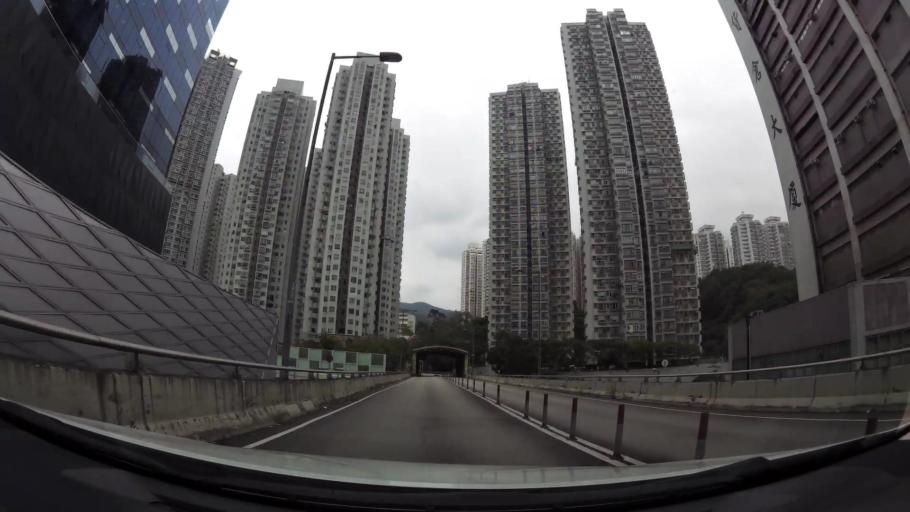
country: HK
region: Tsuen Wan
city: Tsuen Wan
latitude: 22.3752
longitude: 114.1075
